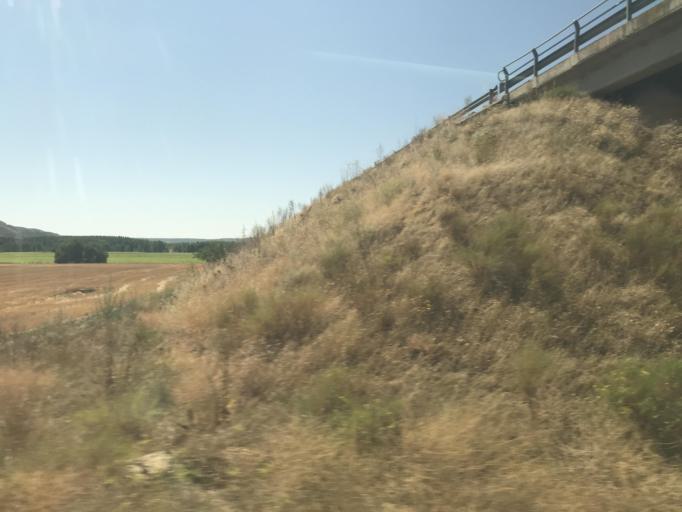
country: ES
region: Castille and Leon
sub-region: Provincia de Palencia
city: Torquemada
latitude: 42.0078
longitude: -4.3444
